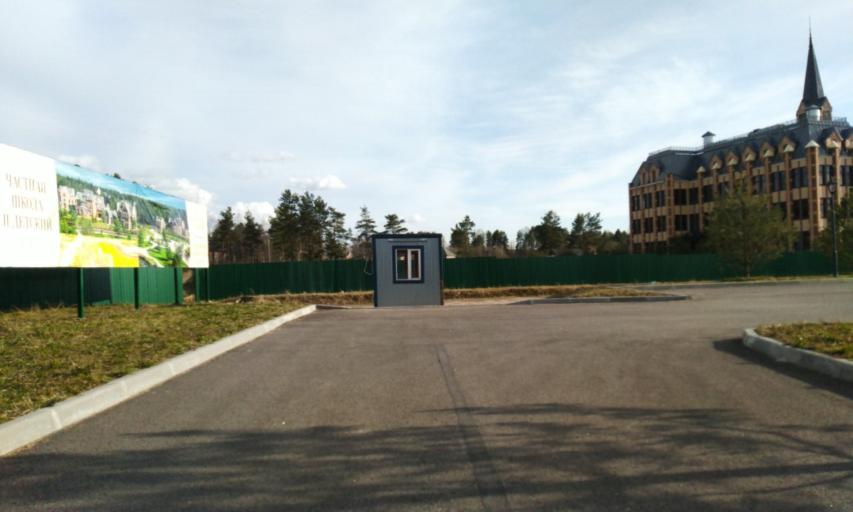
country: RU
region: Leningrad
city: Novoye Devyatkino
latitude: 60.1114
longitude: 30.4485
